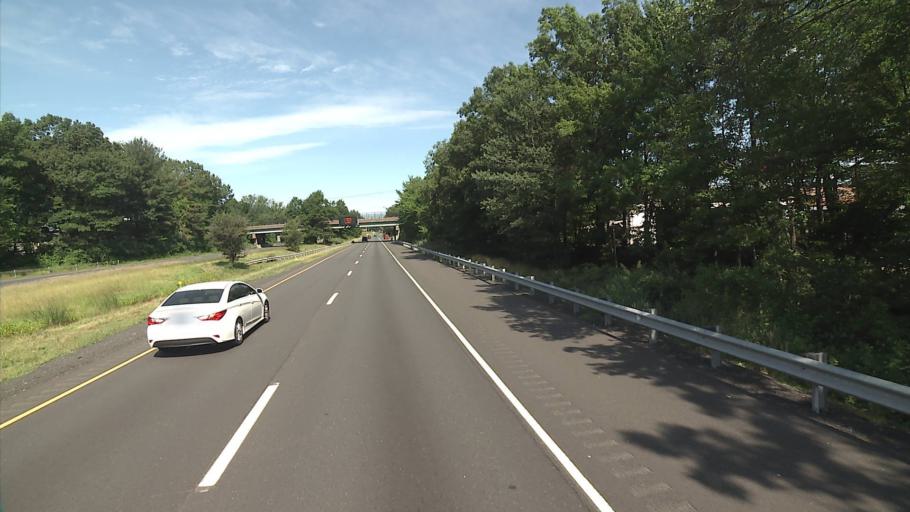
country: US
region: Connecticut
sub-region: Hartford County
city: Glastonbury Center
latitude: 41.7097
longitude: -72.5836
